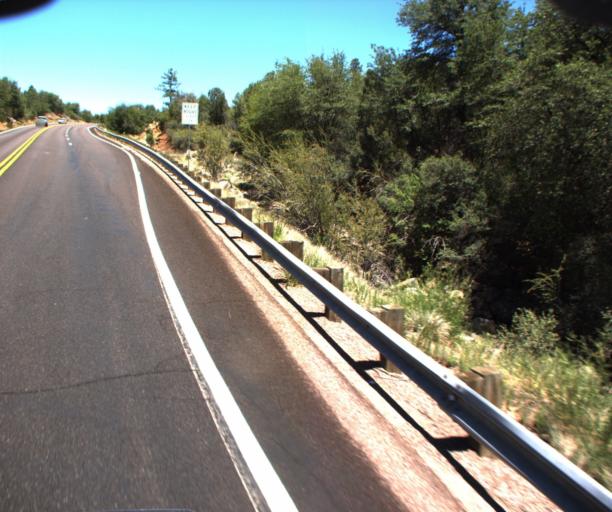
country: US
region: Arizona
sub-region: Gila County
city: Pine
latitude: 34.3215
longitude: -111.4162
